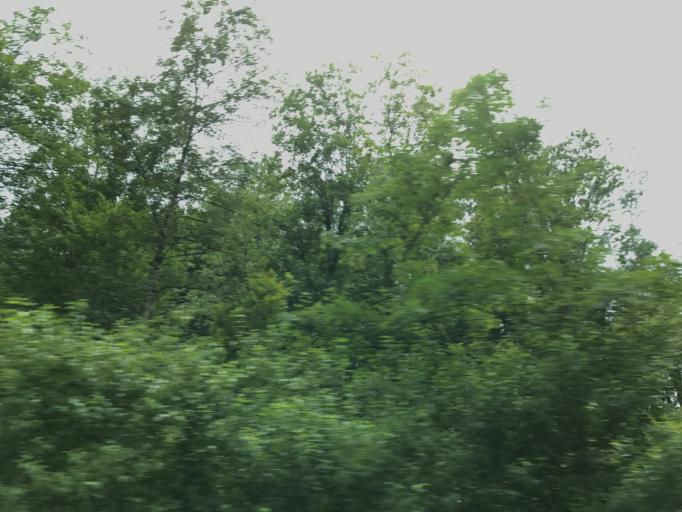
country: DE
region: Baden-Wuerttemberg
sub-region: Tuebingen Region
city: Berg
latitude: 47.8596
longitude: 9.5894
